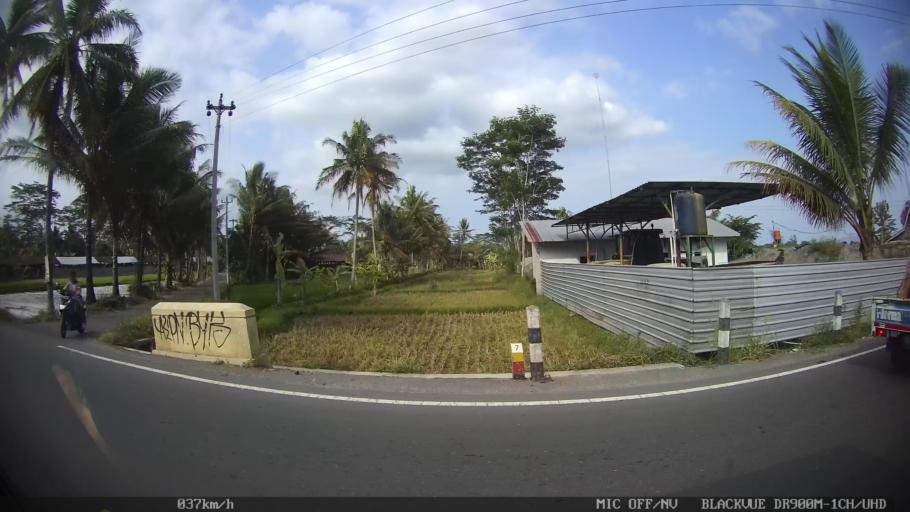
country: ID
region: Central Java
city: Candi Prambanan
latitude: -7.6866
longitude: 110.4609
